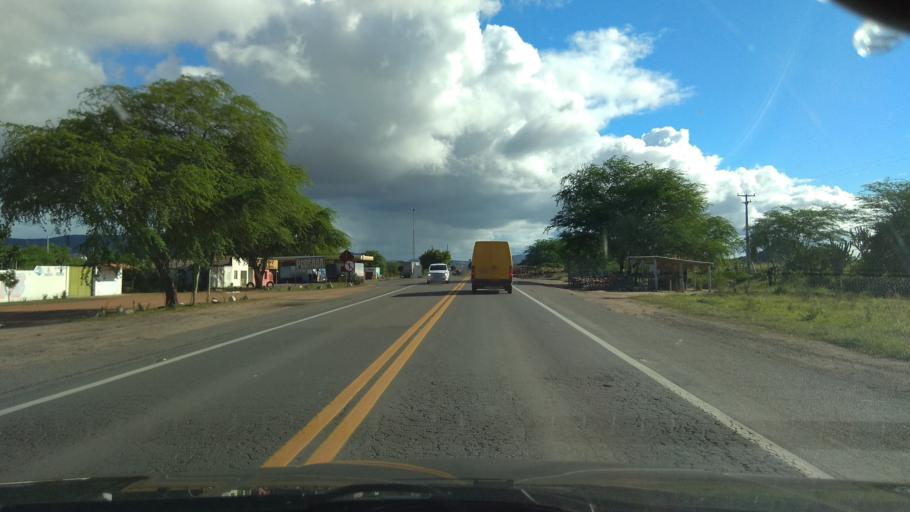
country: BR
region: Bahia
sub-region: Castro Alves
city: Castro Alves
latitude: -12.6838
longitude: -39.6778
